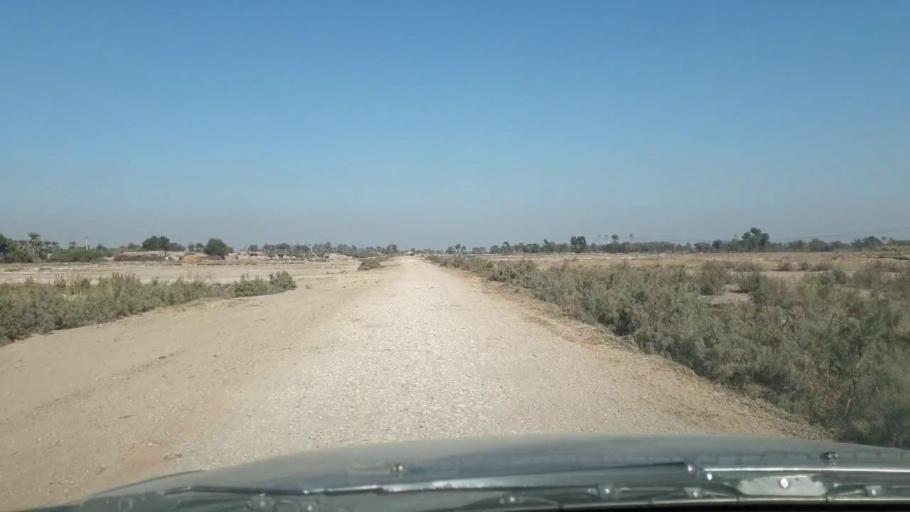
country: PK
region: Sindh
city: Adilpur
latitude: 27.8827
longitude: 69.2721
